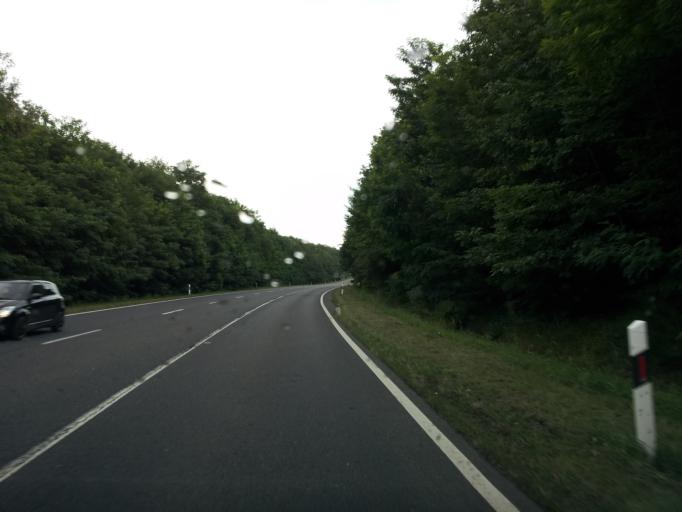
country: HU
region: Vas
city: Sarvar
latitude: 47.1068
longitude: 16.9772
